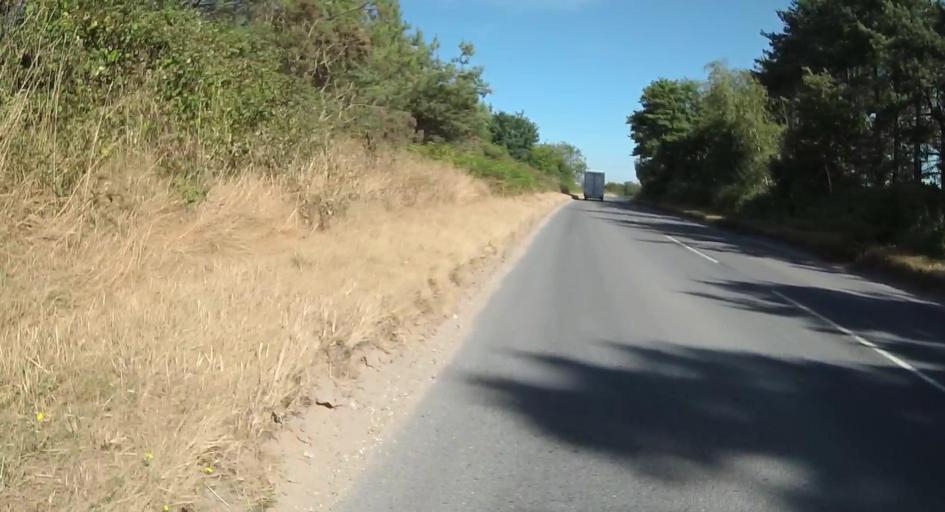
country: GB
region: England
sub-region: Dorset
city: Wool
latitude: 50.6993
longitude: -2.1909
